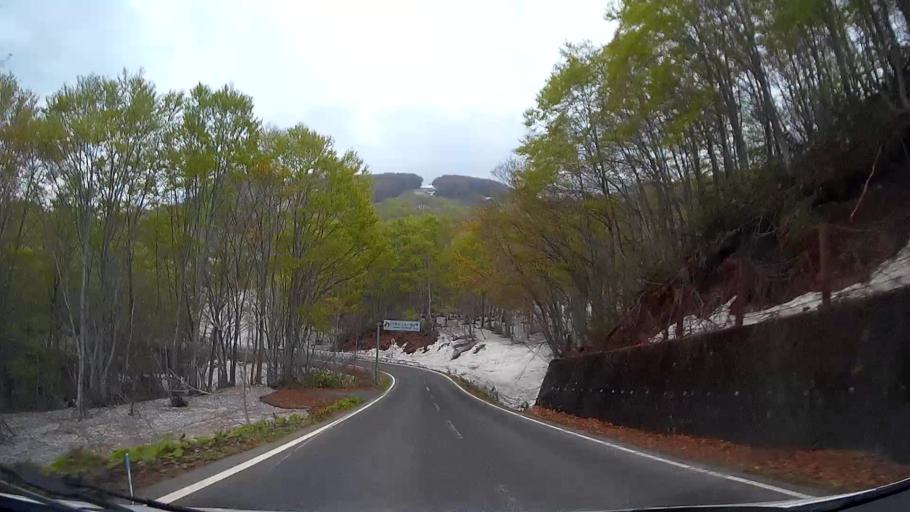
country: JP
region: Aomori
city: Aomori Shi
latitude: 40.6784
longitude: 140.8279
